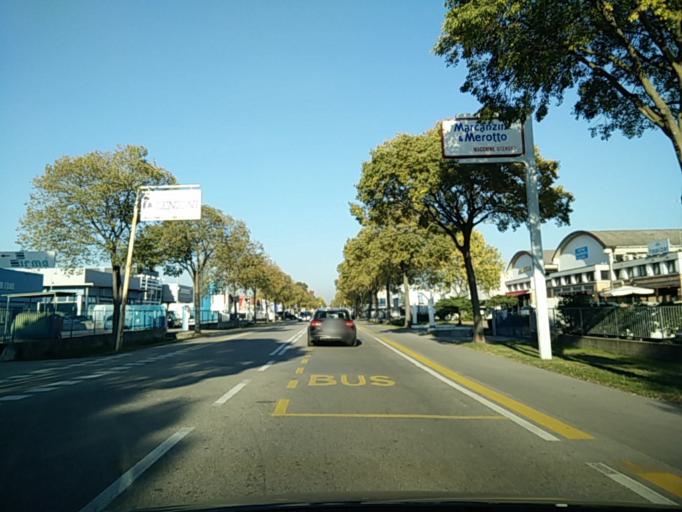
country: IT
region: Veneto
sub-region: Provincia di Treviso
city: Treviso
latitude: 45.6872
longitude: 12.2464
